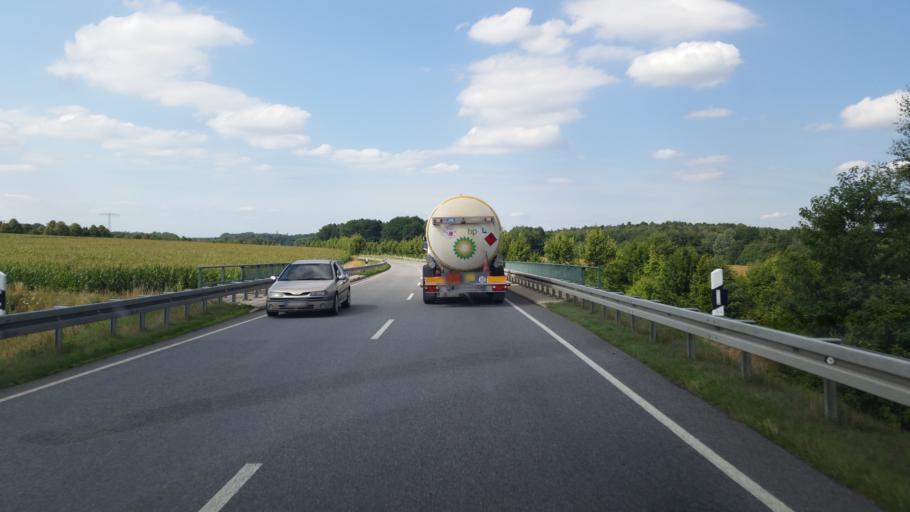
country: DE
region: Saxony
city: Nebelschutz
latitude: 51.2467
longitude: 14.1677
